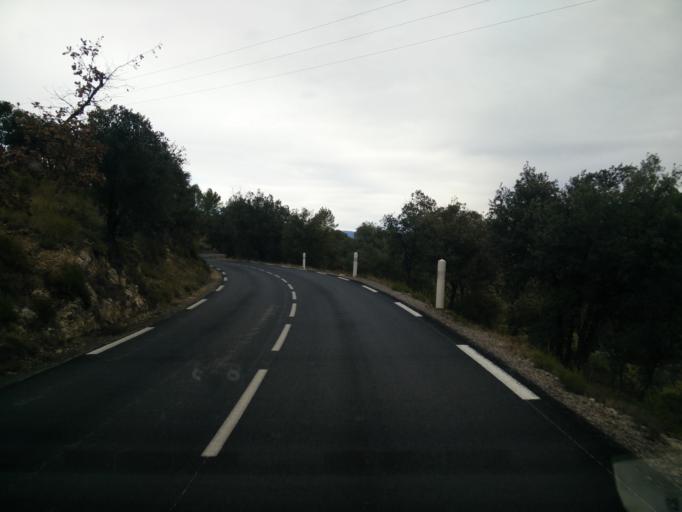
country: FR
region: Provence-Alpes-Cote d'Azur
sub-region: Departement du Var
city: Le Val
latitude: 43.4584
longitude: 6.1050
